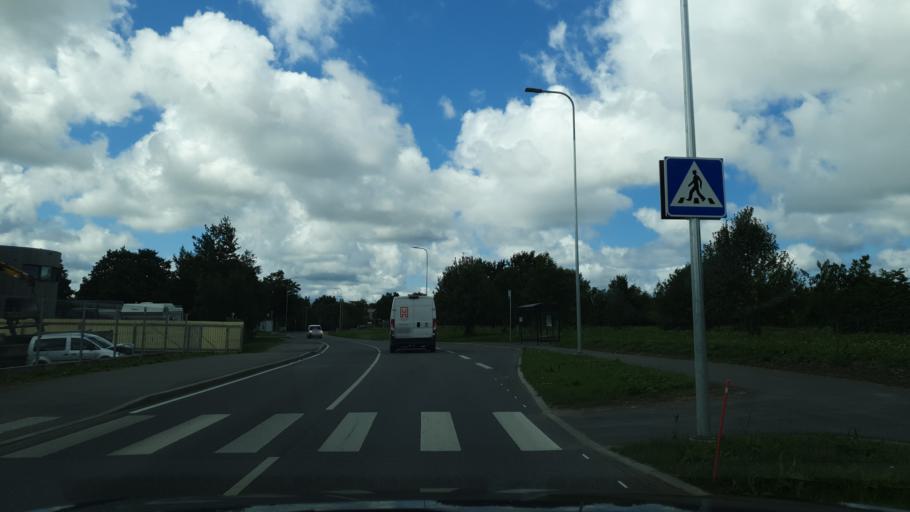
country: EE
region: Harju
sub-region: Viimsi vald
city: Viimsi
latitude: 59.5027
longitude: 24.8459
